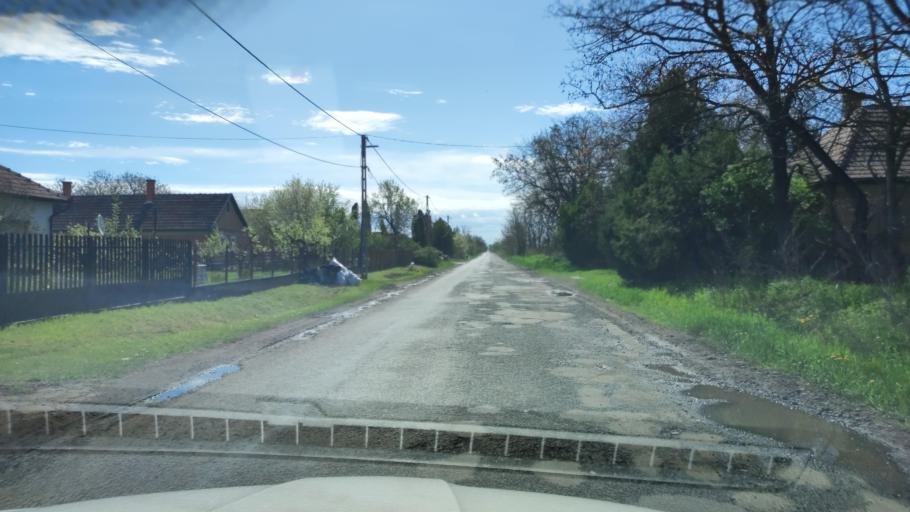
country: HU
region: Pest
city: Abony
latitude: 47.1712
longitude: 20.0287
